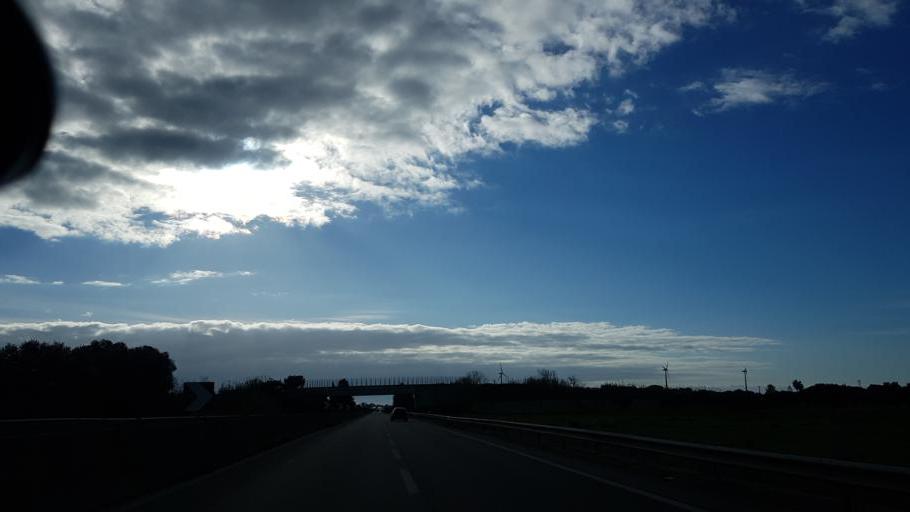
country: IT
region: Apulia
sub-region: Provincia di Brindisi
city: La Rosa
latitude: 40.5782
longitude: 17.9796
